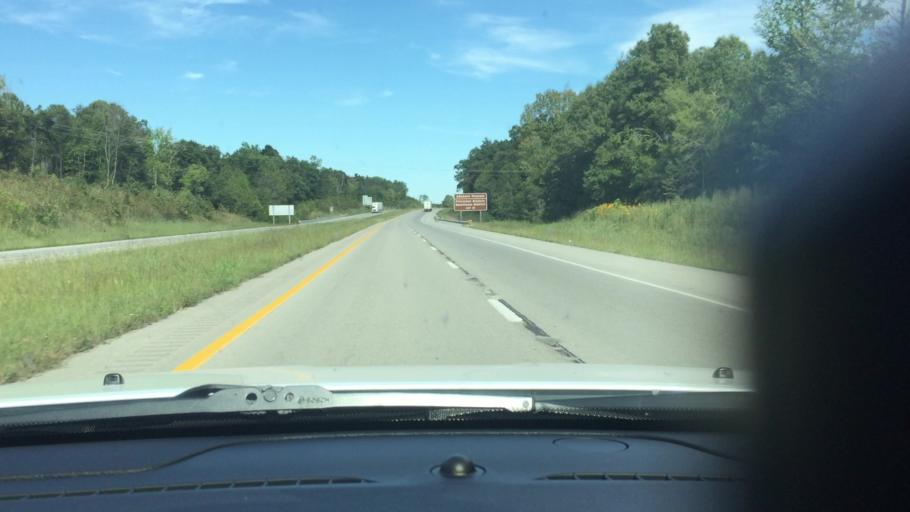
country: US
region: Kentucky
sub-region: Caldwell County
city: Princeton
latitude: 37.1276
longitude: -87.8822
